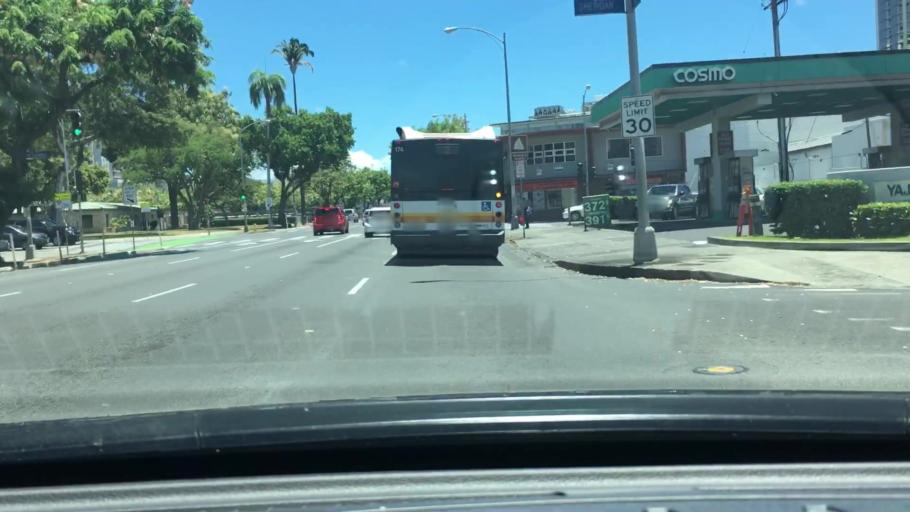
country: US
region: Hawaii
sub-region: Honolulu County
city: Honolulu
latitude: 21.2986
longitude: -157.8408
